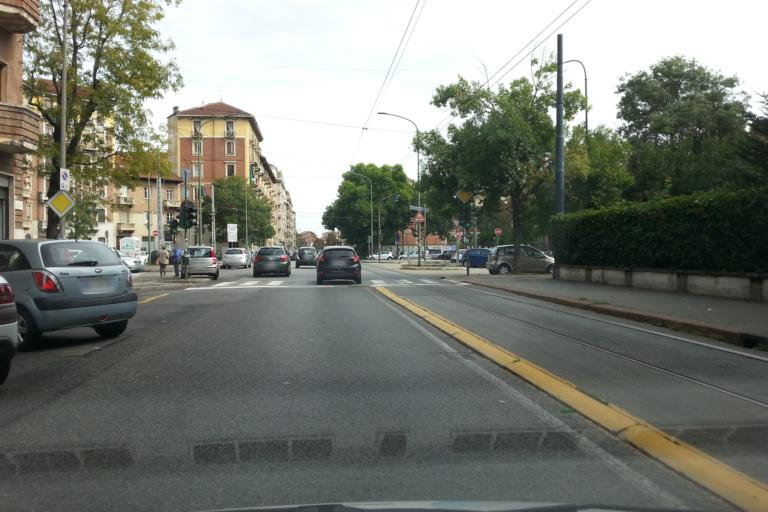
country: IT
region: Piedmont
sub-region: Provincia di Torino
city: Moncalieri
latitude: 45.0336
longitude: 7.6700
